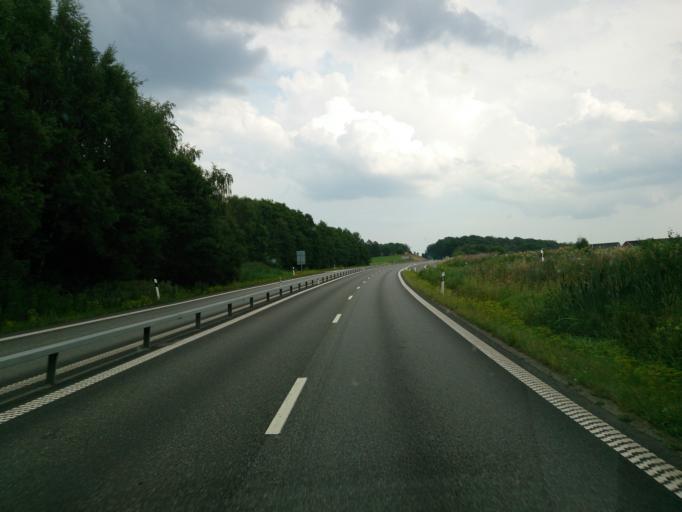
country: SE
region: Skane
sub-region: Horby Kommun
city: Hoerby
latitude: 55.8659
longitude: 13.6638
